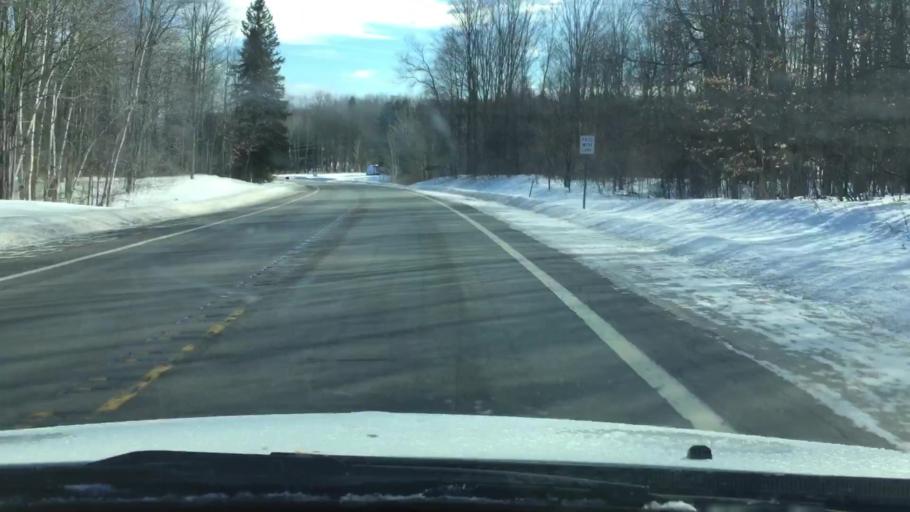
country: US
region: Michigan
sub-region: Antrim County
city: Mancelona
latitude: 44.9909
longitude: -85.0614
